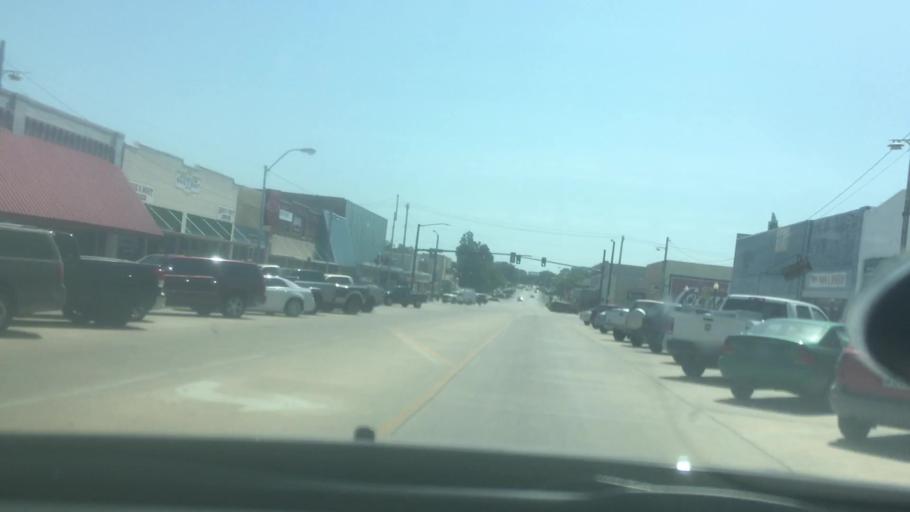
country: US
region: Oklahoma
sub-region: Pontotoc County
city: Ada
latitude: 34.7745
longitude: -96.6767
